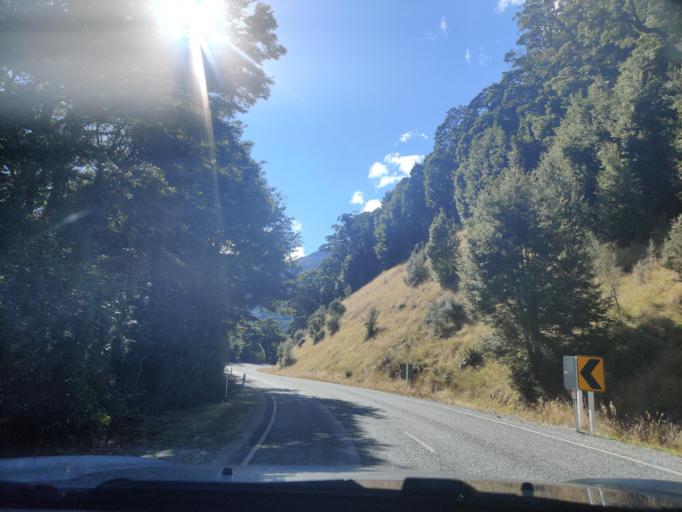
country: NZ
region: Otago
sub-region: Queenstown-Lakes District
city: Wanaka
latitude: -44.1491
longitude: 169.3141
